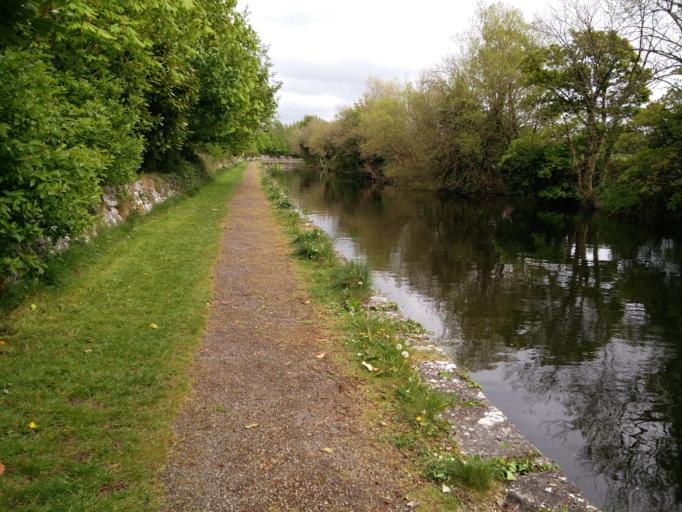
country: IE
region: Connaught
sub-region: Maigh Eo
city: Ballinrobe
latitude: 53.6226
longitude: -9.2340
